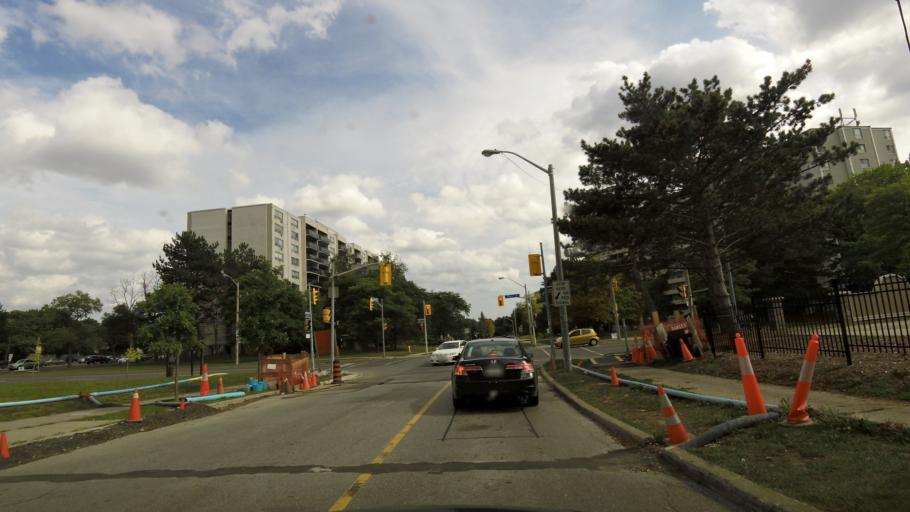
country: CA
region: Ontario
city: Etobicoke
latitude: 43.6295
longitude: -79.5802
